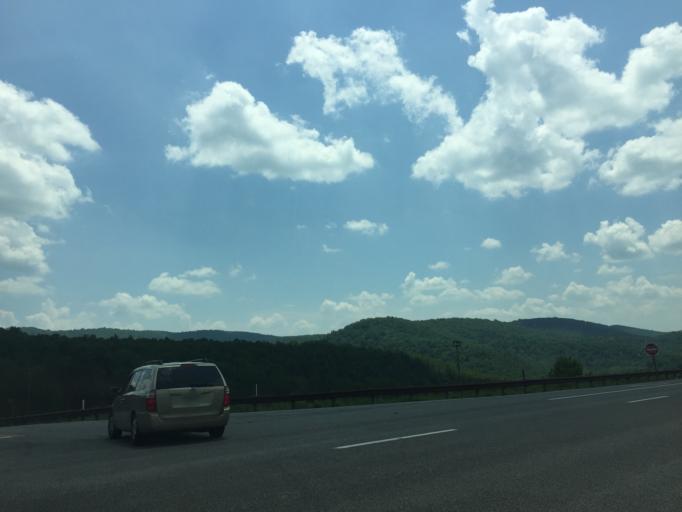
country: US
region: Virginia
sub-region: Shenandoah County
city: Woodstock
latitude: 39.0516
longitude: -78.6987
